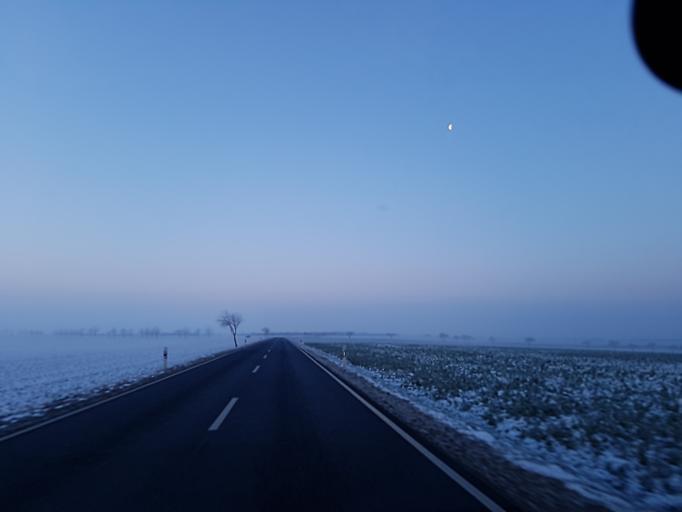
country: DE
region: Saxony
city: Strehla
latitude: 51.3319
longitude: 13.2062
